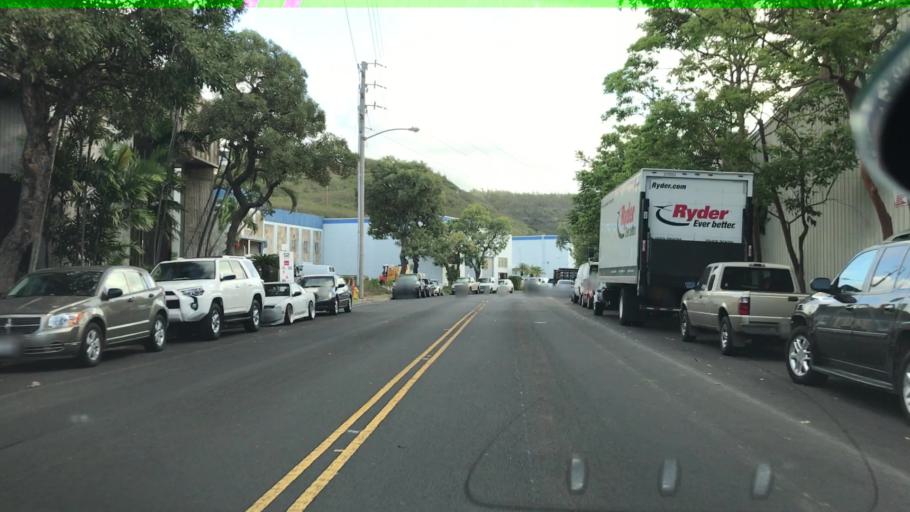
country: US
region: Hawaii
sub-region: Honolulu County
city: Halawa Heights
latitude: 21.3734
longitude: -157.9133
